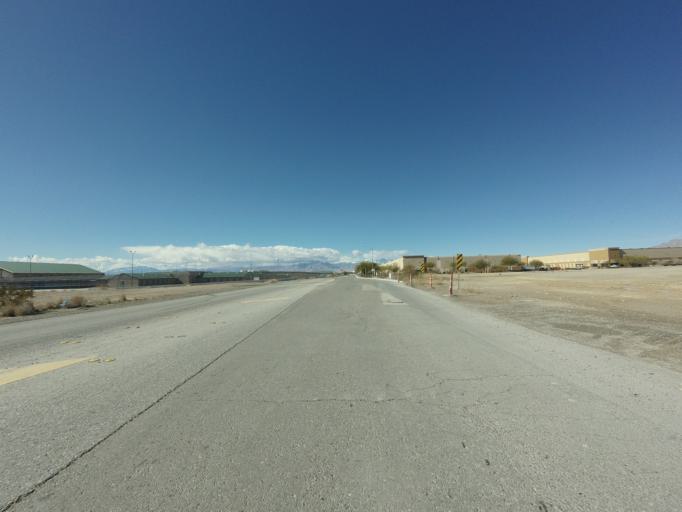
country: US
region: Nevada
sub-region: Clark County
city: Nellis Air Force Base
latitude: 36.2659
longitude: -115.0521
